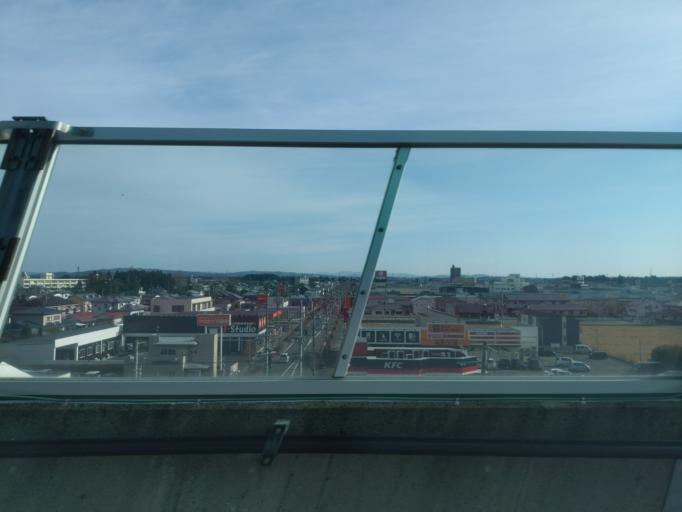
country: JP
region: Miyagi
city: Furukawa
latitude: 38.5755
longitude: 140.9691
